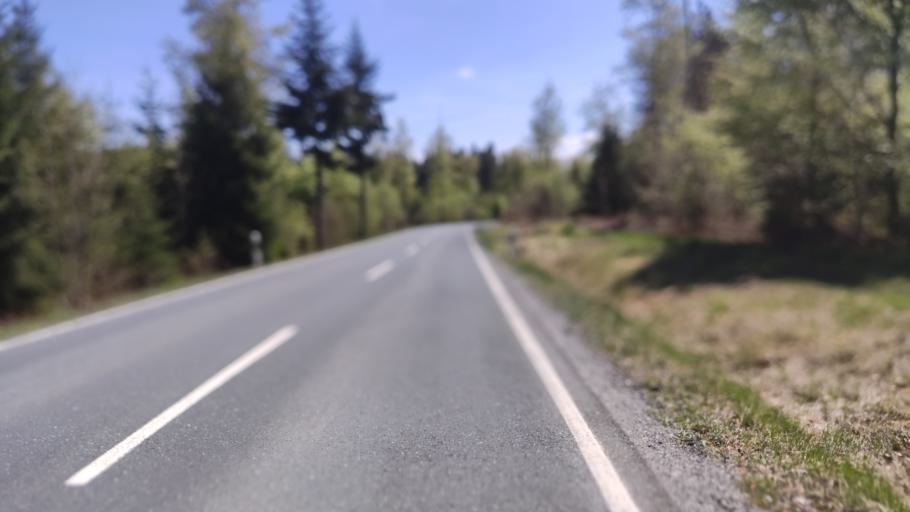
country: DE
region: Bavaria
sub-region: Upper Franconia
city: Nordhalben
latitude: 50.3580
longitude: 11.4704
